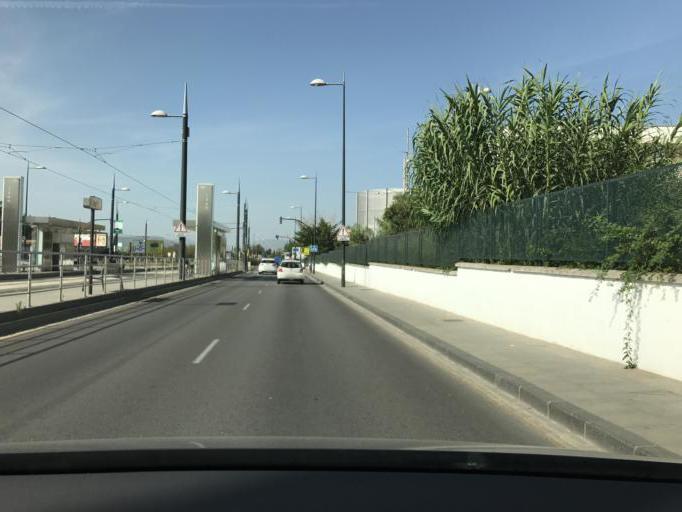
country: ES
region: Andalusia
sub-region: Provincia de Granada
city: Maracena
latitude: 37.2038
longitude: -3.6168
